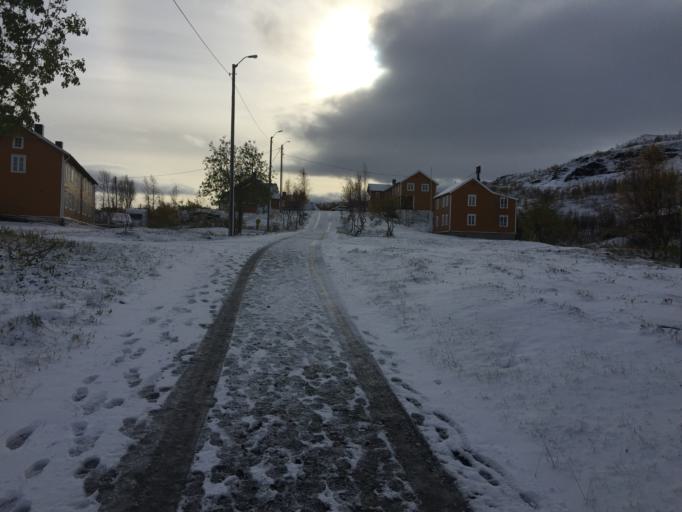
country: NO
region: Nordland
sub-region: Sorfold
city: Straumen
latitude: 67.0957
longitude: 16.0063
